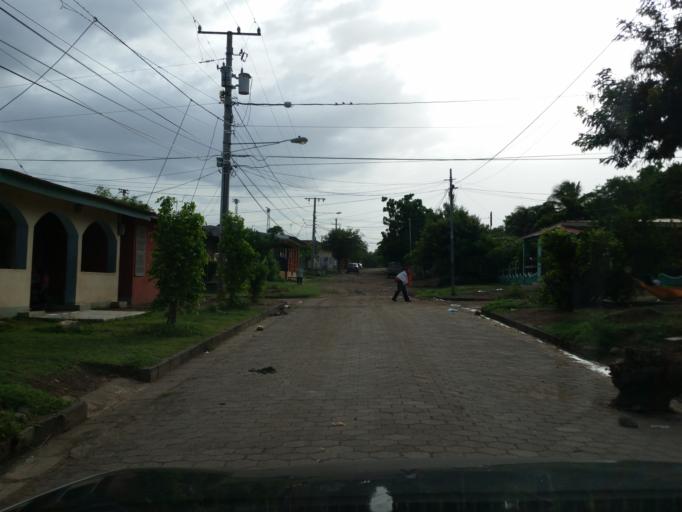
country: NI
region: Granada
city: Granada
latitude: 11.9394
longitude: -85.9608
